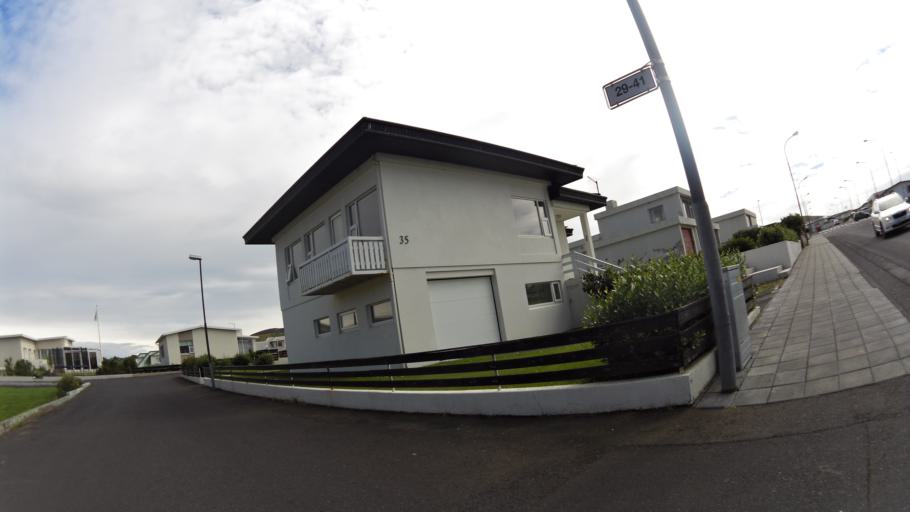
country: IS
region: South
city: Vestmannaeyjar
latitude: 63.4370
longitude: -20.2818
